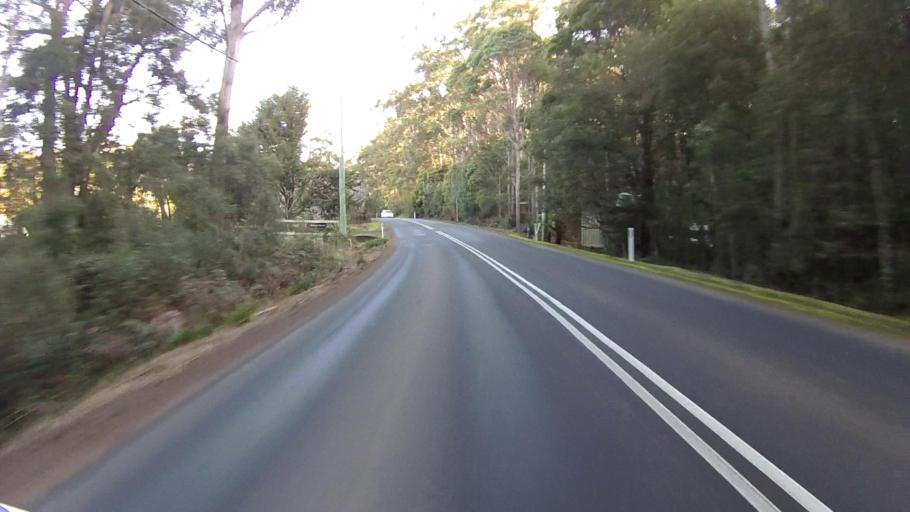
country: AU
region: Tasmania
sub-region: Clarence
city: Sandford
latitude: -43.1191
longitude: 147.8510
